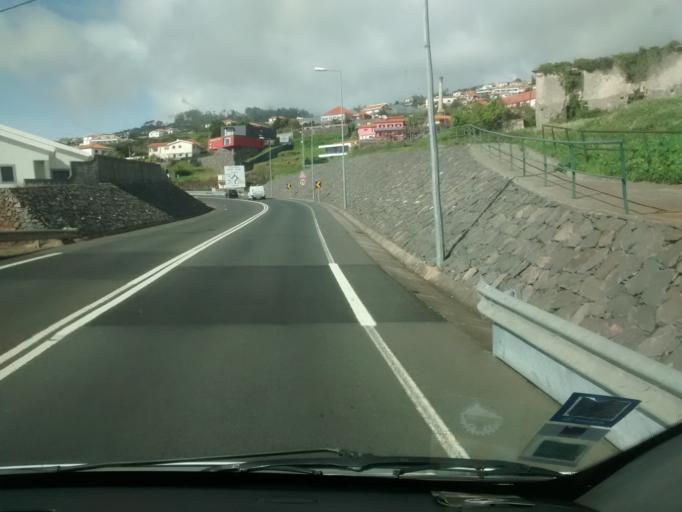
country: PT
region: Madeira
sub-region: Calheta
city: Estreito da Calheta
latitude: 32.7314
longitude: -17.1899
